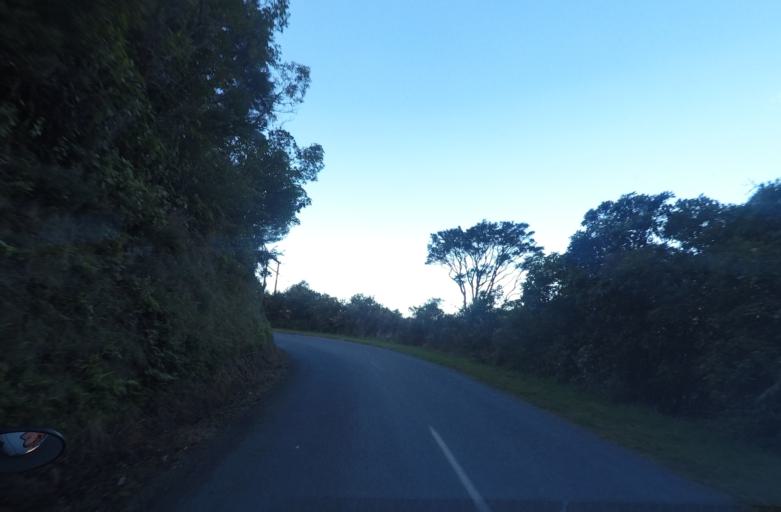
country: NZ
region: Marlborough
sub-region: Marlborough District
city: Picton
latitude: -41.2714
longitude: 173.9583
